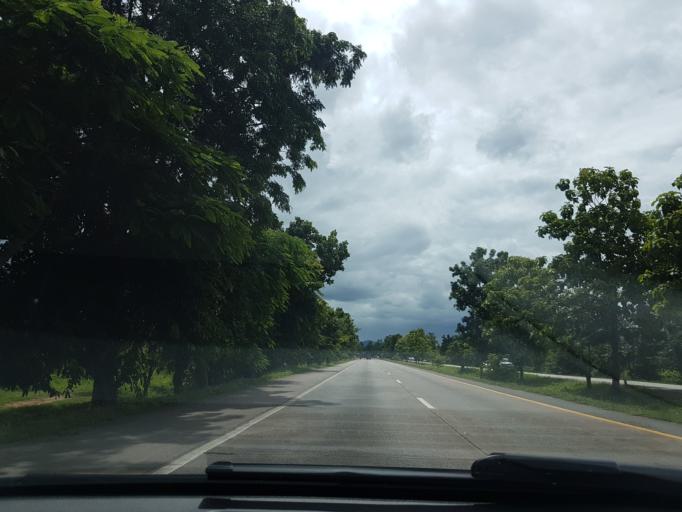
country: TH
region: Lampang
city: Hang Chat
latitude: 18.3204
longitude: 99.3435
